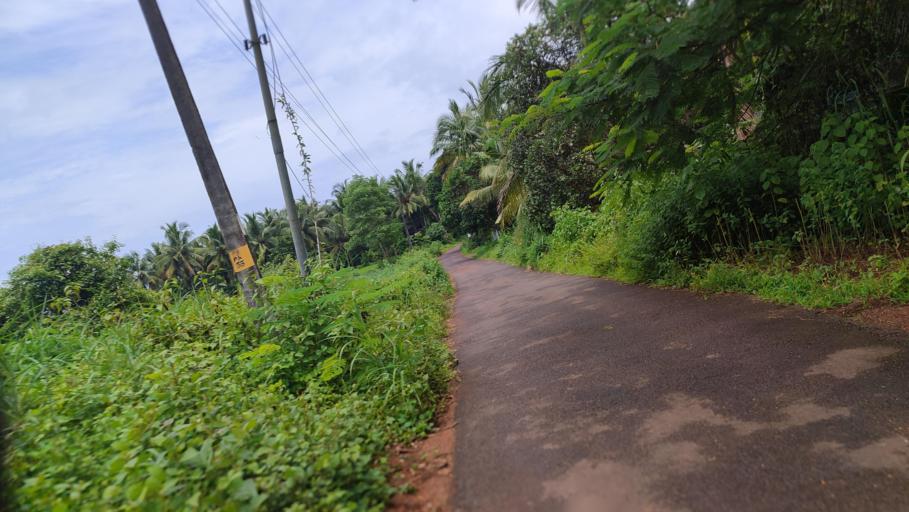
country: IN
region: Kerala
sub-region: Kasaragod District
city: Kannangad
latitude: 12.4011
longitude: 75.0563
